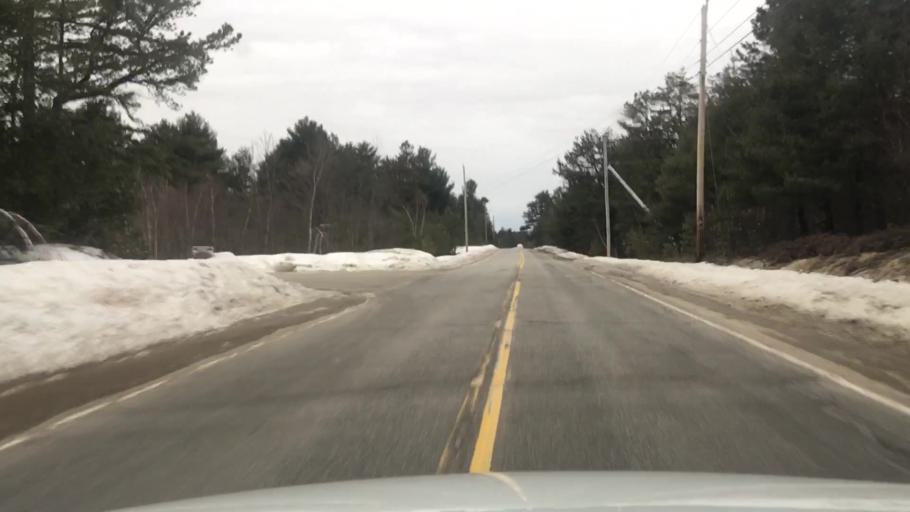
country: US
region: Maine
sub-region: York County
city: Shapleigh
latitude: 43.5737
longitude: -70.8638
